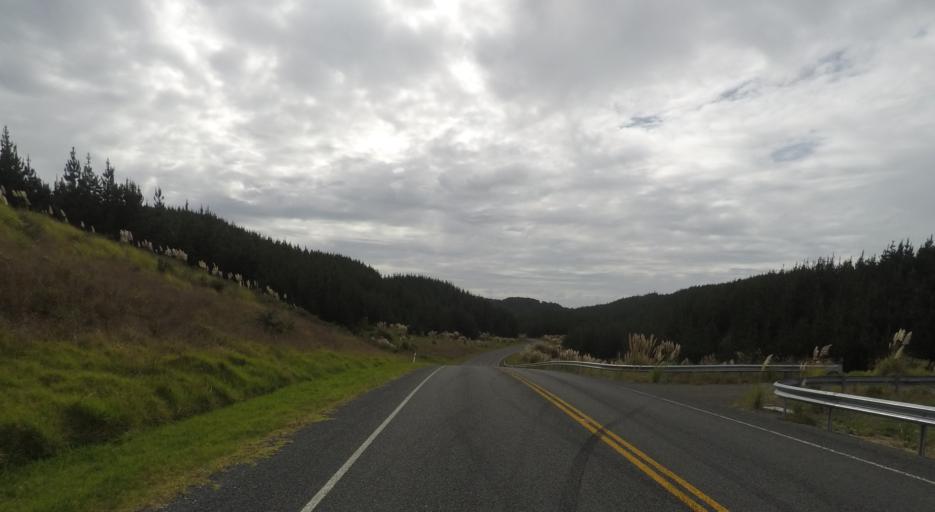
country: NZ
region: Auckland
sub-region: Auckland
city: Rothesay Bay
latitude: -36.6547
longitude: 174.7006
